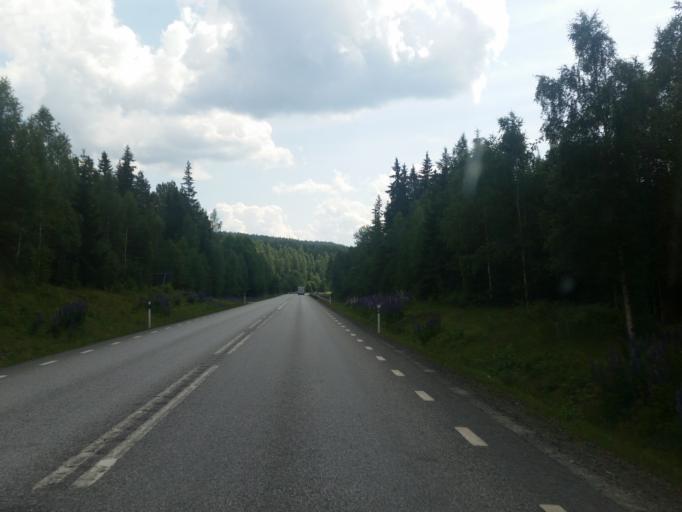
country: SE
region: OErebro
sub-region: Ljusnarsbergs Kommun
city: Kopparberg
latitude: 59.8678
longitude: 15.0530
